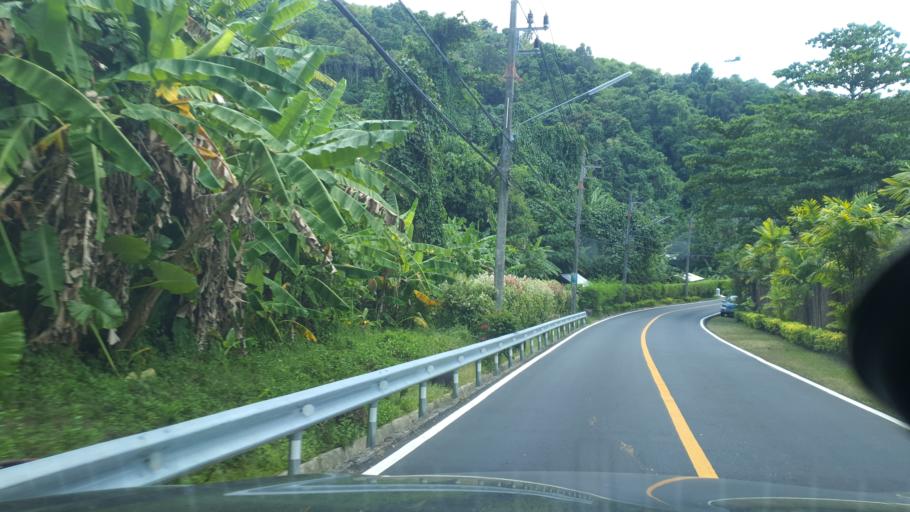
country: TH
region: Phuket
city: Thalang
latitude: 8.0480
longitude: 98.2784
